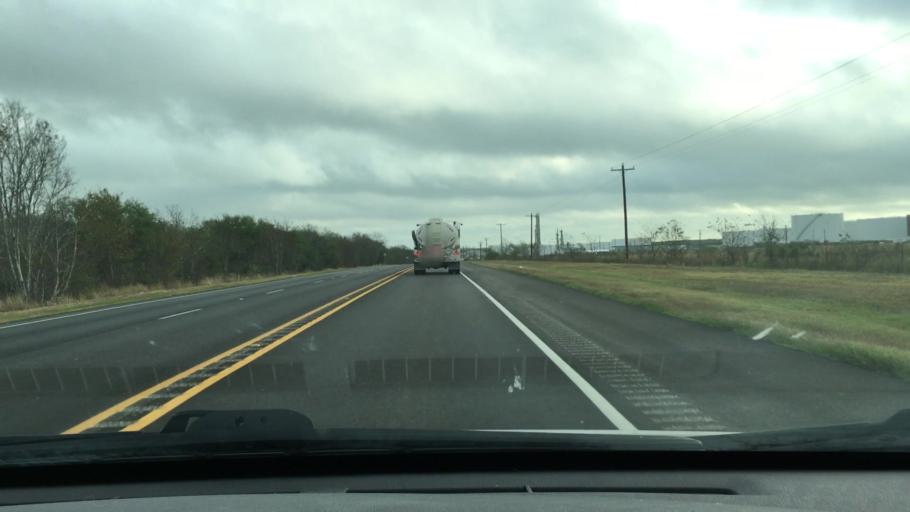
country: US
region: Texas
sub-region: Gonzales County
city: Nixon
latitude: 29.2601
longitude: -97.7965
